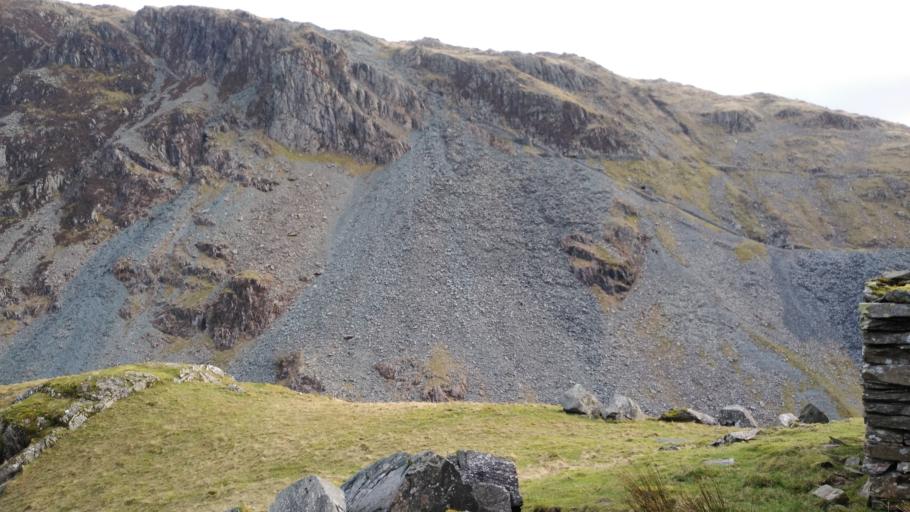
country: GB
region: England
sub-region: Cumbria
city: Keswick
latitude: 54.5146
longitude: -3.2070
